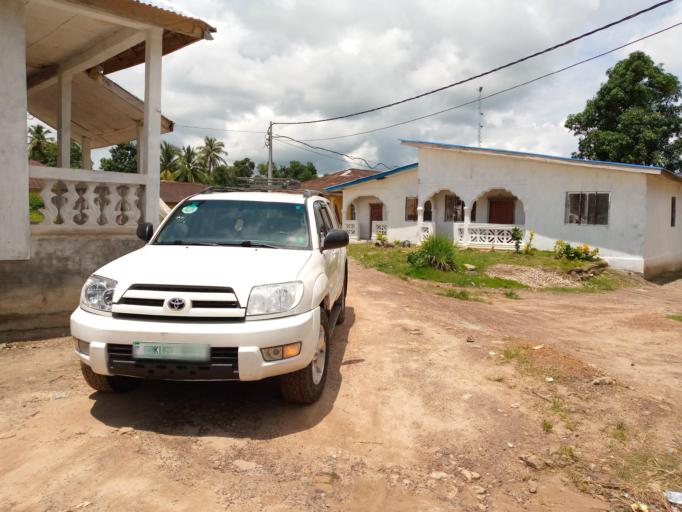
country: SL
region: Northern Province
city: Magburaka
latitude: 8.7218
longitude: -11.9475
